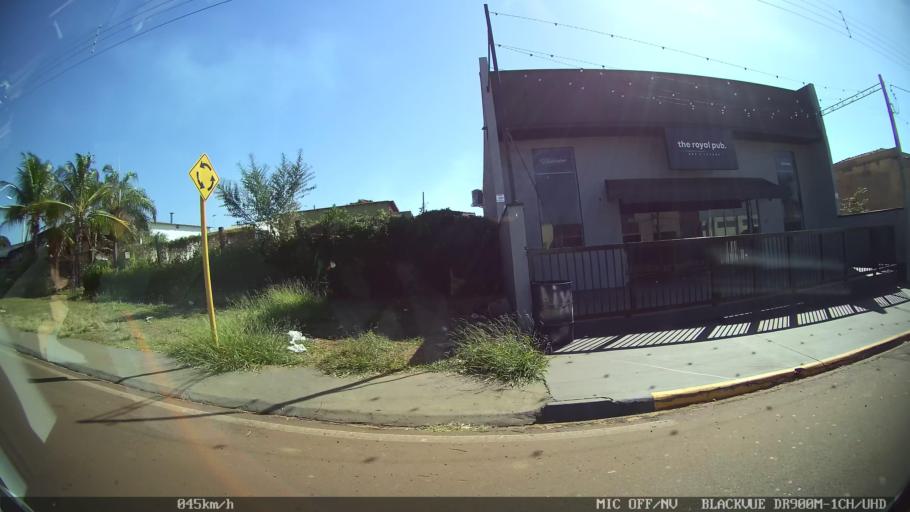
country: BR
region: Sao Paulo
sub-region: Batatais
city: Batatais
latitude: -20.8843
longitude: -47.5989
